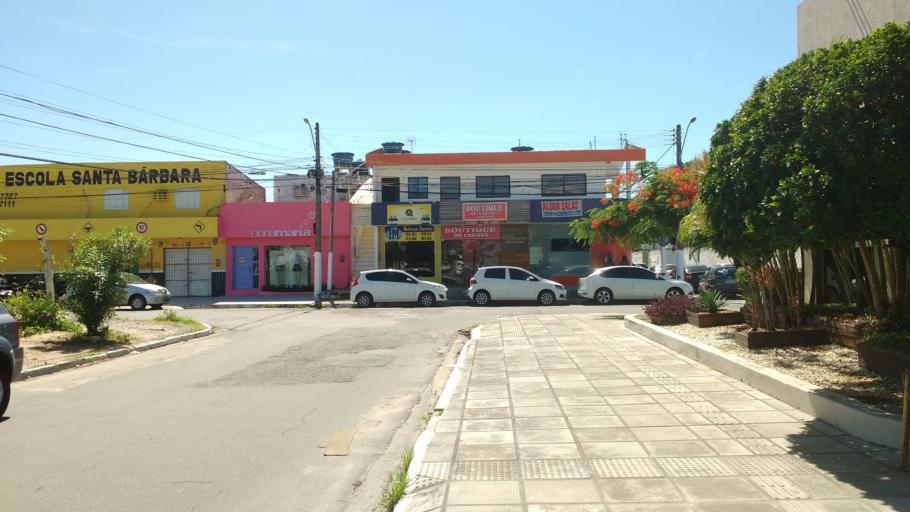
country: BR
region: Alagoas
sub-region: Maceio
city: Maceio
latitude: -9.6529
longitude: -35.7039
